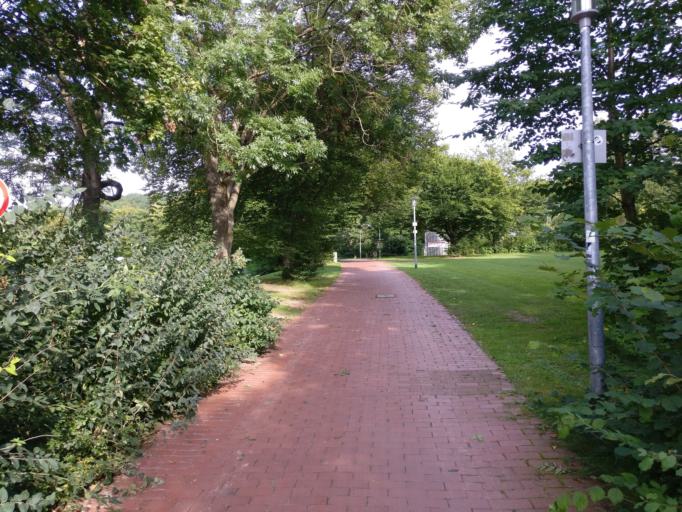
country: DE
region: Lower Saxony
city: Goettingen
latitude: 51.5485
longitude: 9.9501
